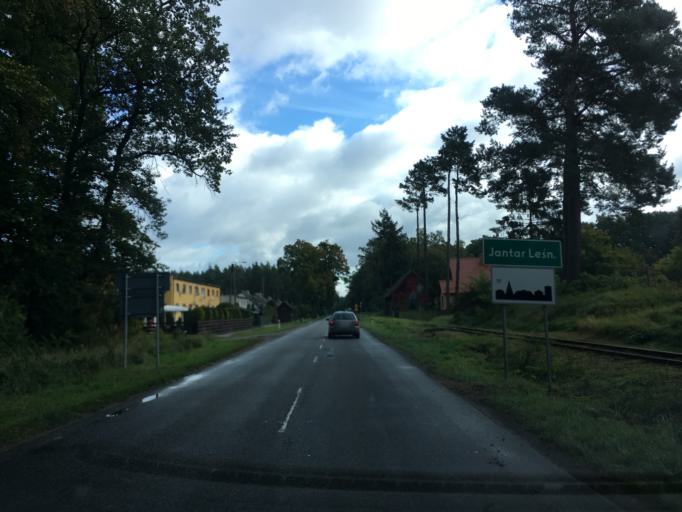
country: PL
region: Pomeranian Voivodeship
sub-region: Powiat nowodworski
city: Stegna
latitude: 54.3345
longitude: 19.0000
